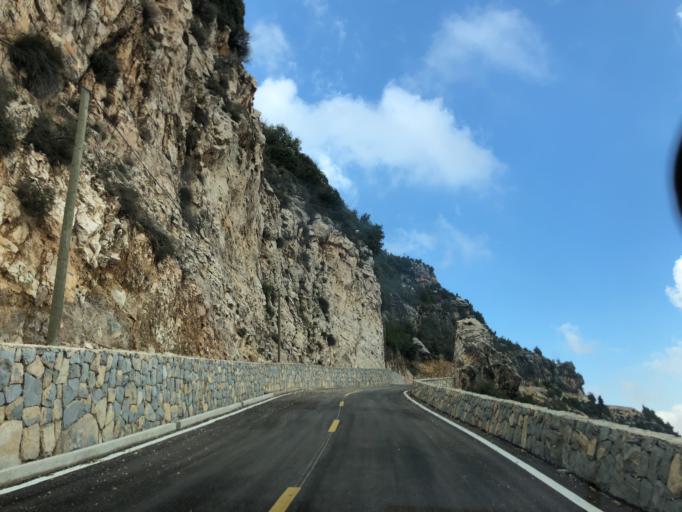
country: LB
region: Liban-Nord
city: Amioun
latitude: 34.2094
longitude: 35.8310
